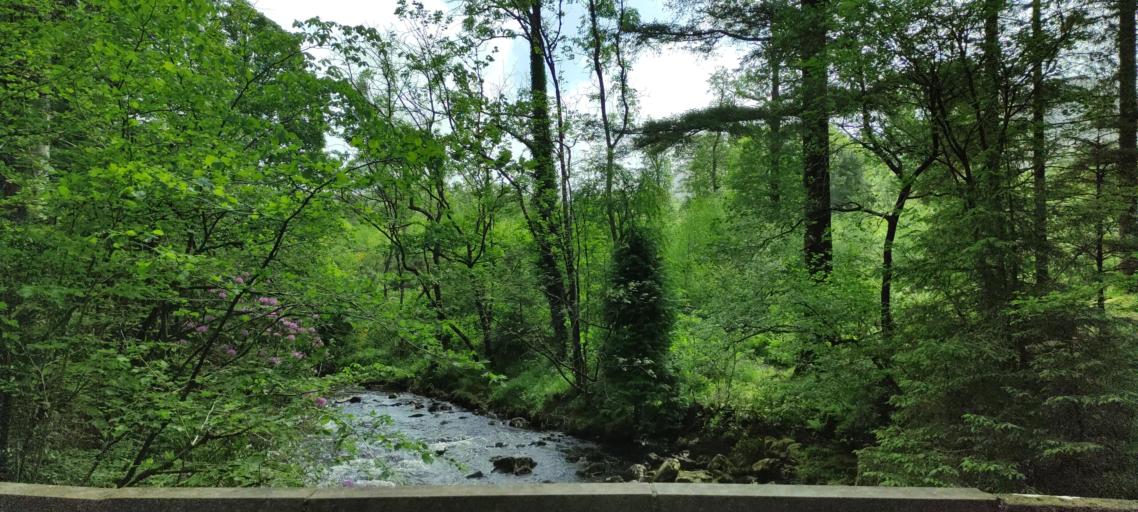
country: GB
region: England
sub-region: Cumbria
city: Millom
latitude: 54.3922
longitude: -3.2774
